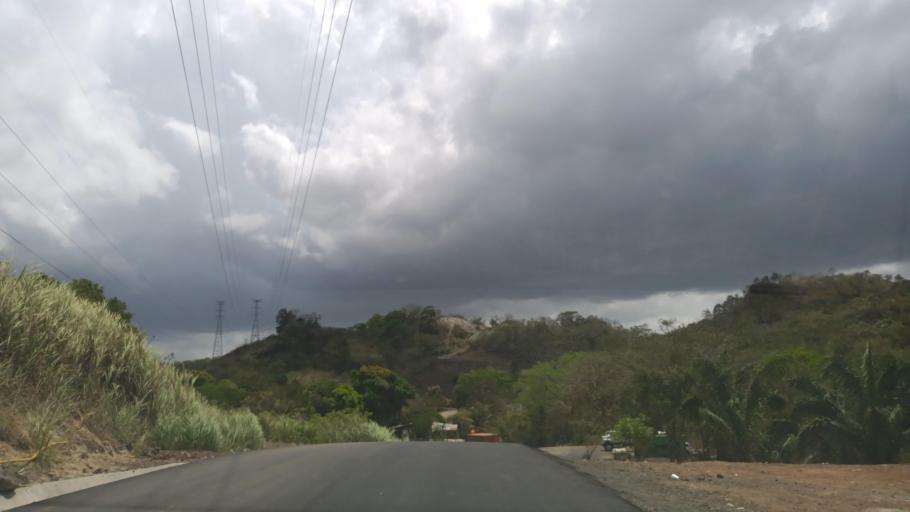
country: PA
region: Panama
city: Alcalde Diaz
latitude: 9.0820
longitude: -79.5763
